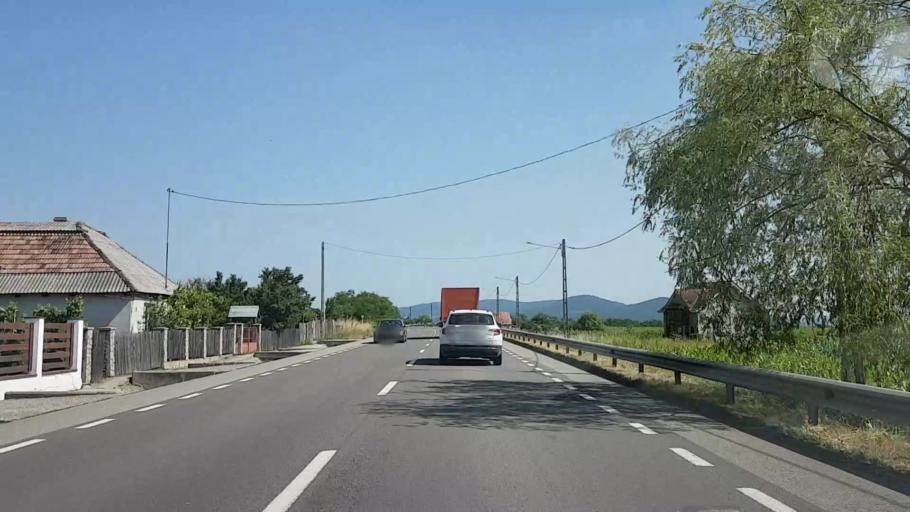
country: RO
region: Bistrita-Nasaud
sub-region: Comuna Sieu-Odorhei
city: Sieu-Odorhei
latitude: 47.1326
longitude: 24.3105
